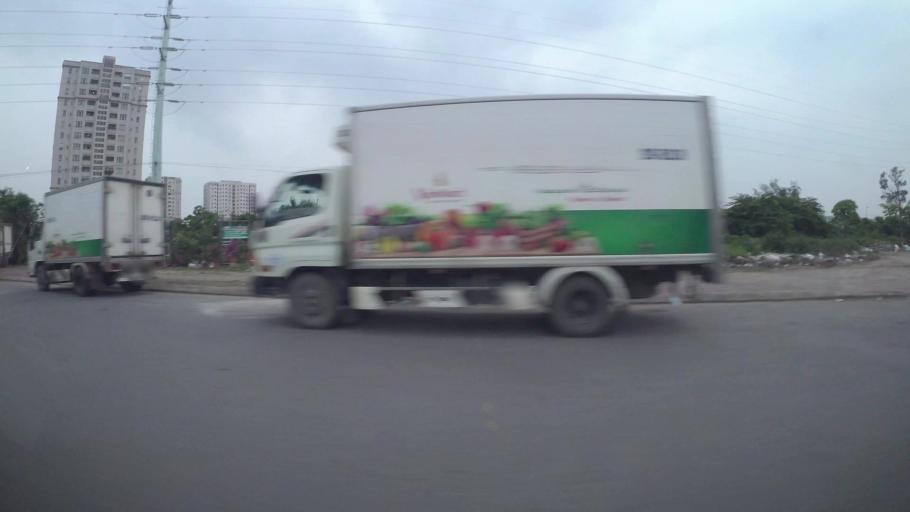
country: VN
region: Ha Noi
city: Trau Quy
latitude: 21.0411
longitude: 105.9133
